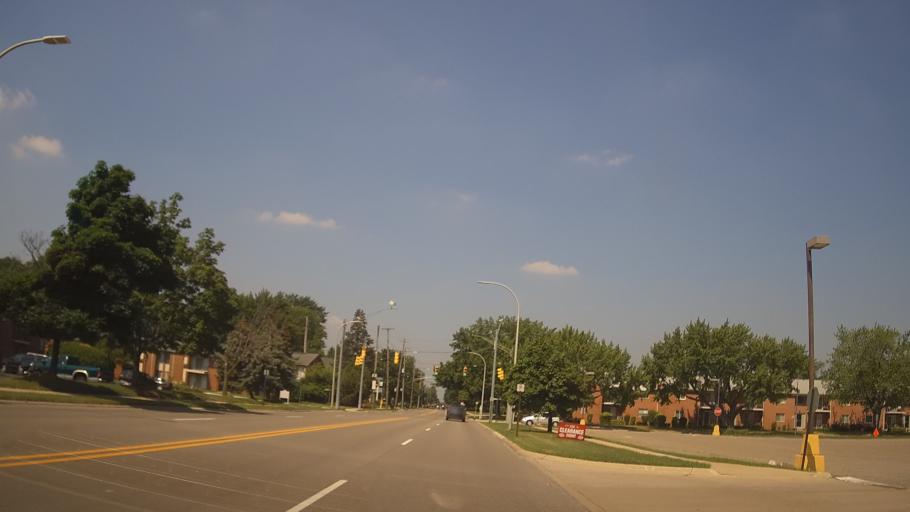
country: US
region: Michigan
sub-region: Macomb County
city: Fraser
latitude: 42.5323
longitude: -82.9181
